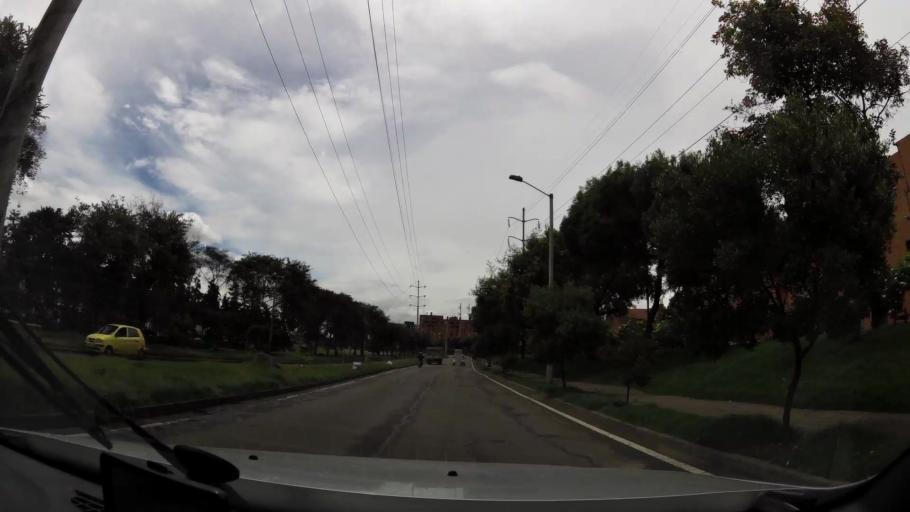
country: CO
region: Bogota D.C.
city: Bogota
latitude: 4.6479
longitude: -74.1095
